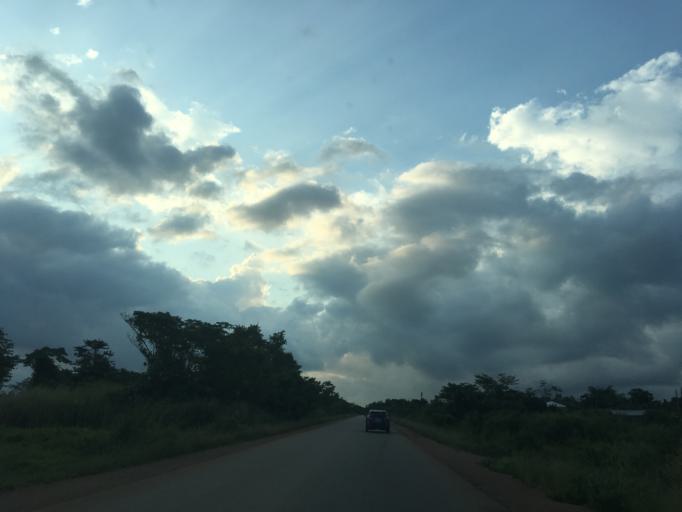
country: GH
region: Western
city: Bibiani
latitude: 6.7090
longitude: -2.4535
